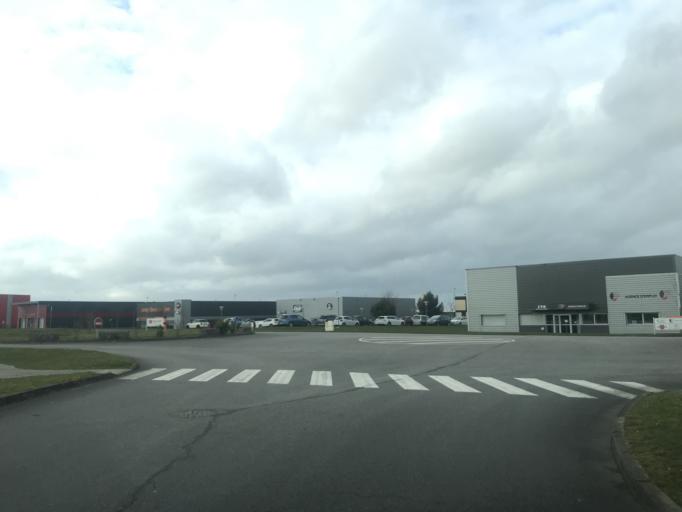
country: FR
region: Lower Normandy
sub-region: Departement du Calvados
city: Cormelles-le-Royal
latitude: 49.1443
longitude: -0.3305
